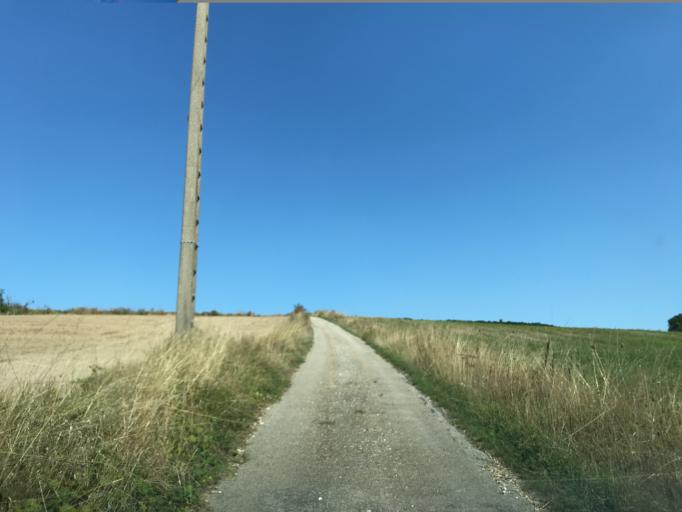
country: FR
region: Haute-Normandie
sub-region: Departement de l'Eure
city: Heudreville-sur-Eure
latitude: 49.1247
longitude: 1.2248
